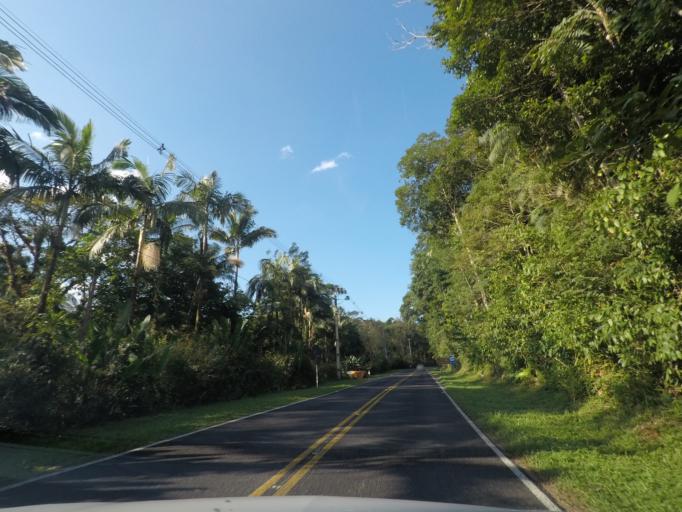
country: BR
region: Parana
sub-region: Antonina
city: Antonina
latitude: -25.4031
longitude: -48.8758
